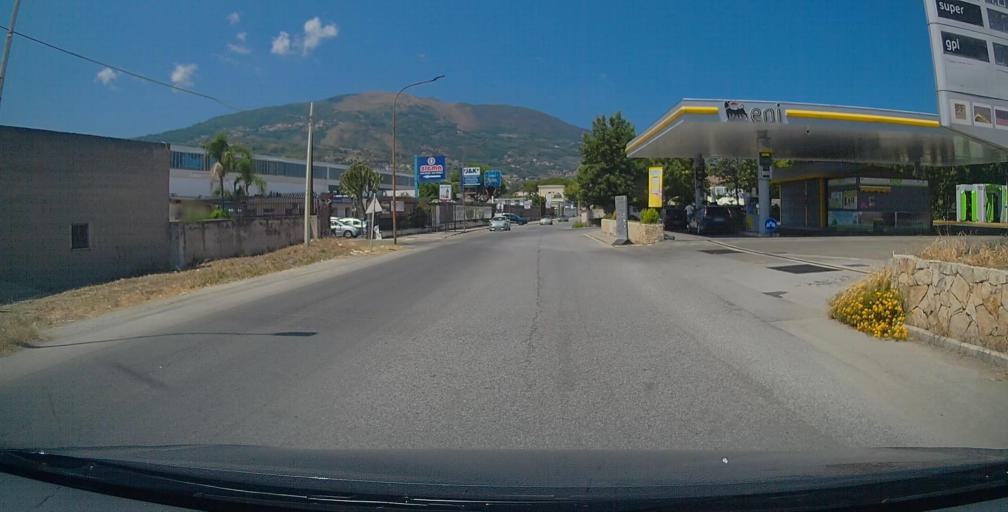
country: IT
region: Sicily
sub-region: Messina
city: Patti
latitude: 38.1487
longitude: 14.9806
